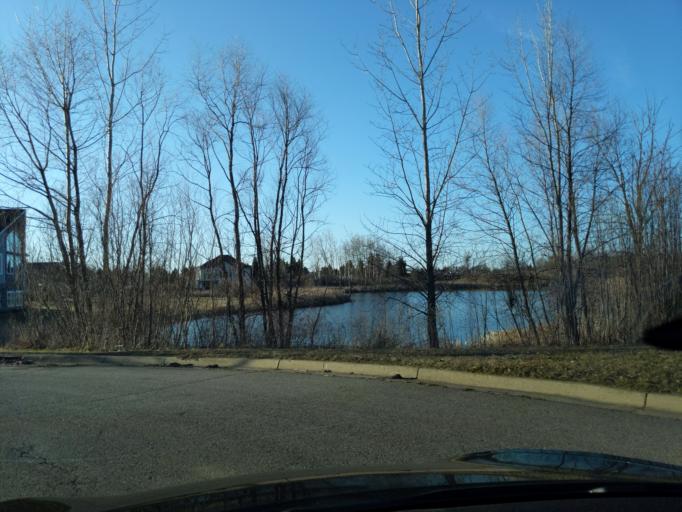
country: US
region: Michigan
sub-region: Ingham County
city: Mason
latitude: 42.5947
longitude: -84.4440
